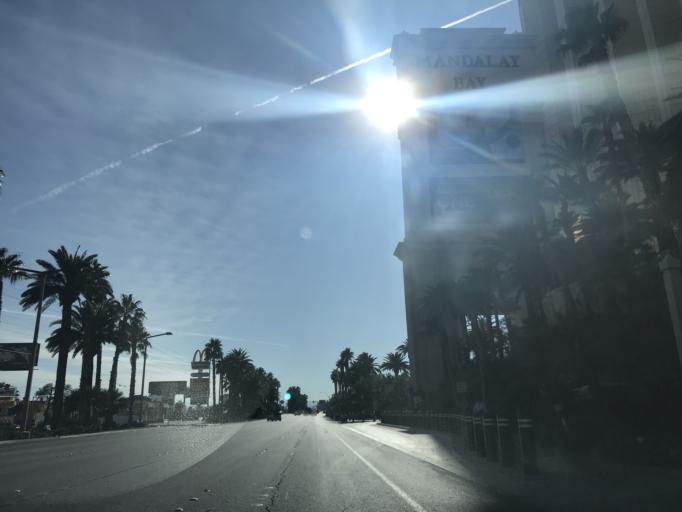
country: US
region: Nevada
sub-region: Clark County
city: Paradise
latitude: 36.0927
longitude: -115.1731
